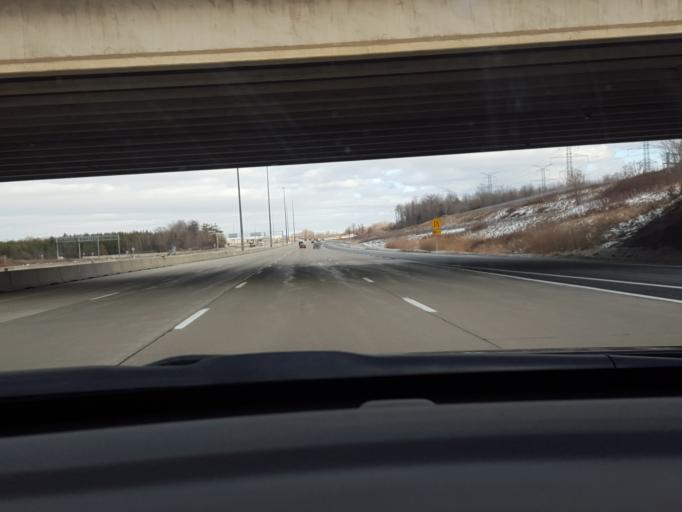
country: CA
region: Ontario
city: Markham
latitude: 43.8560
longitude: -79.2820
